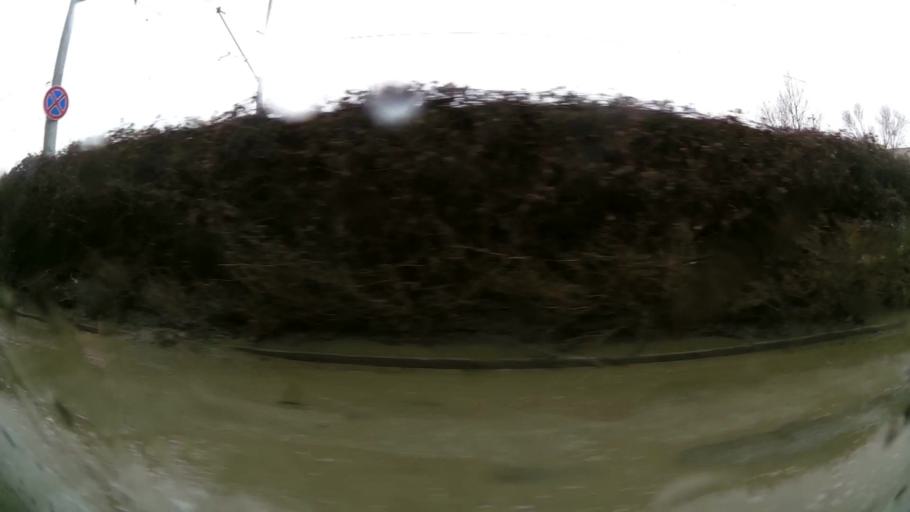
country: BG
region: Sofia-Capital
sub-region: Stolichna Obshtina
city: Sofia
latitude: 42.6589
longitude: 23.4150
